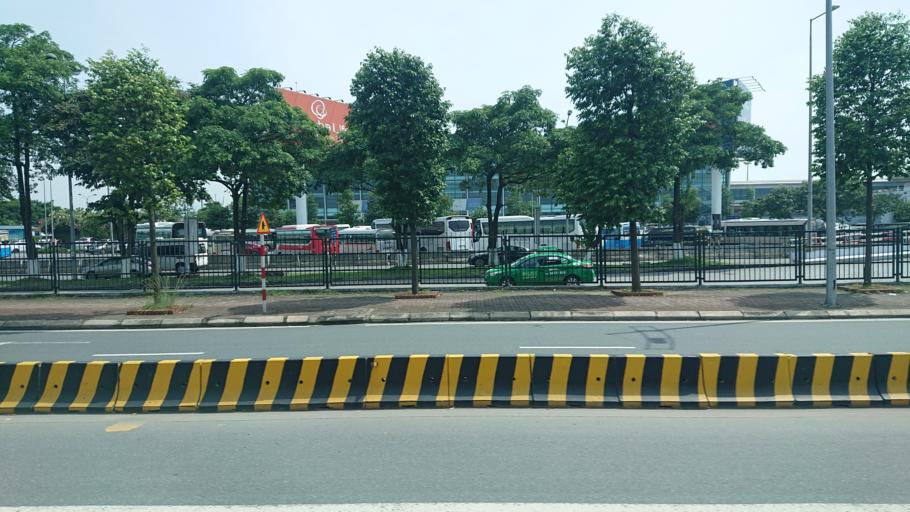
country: VN
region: Ha Noi
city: Soc Son
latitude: 21.2138
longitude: 105.8005
